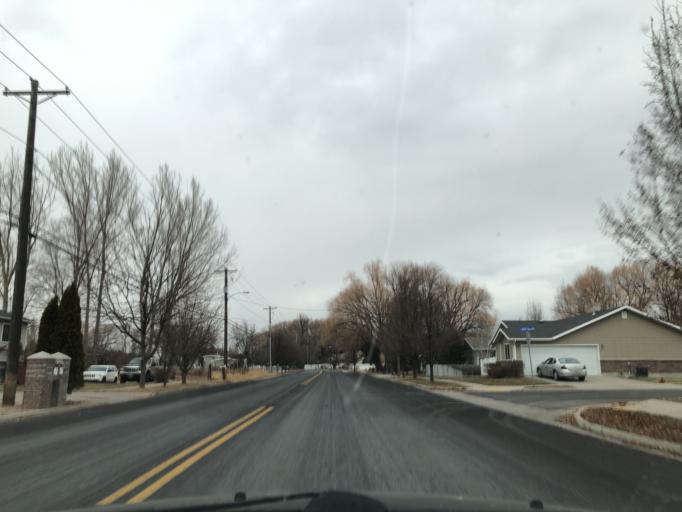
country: US
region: Utah
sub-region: Cache County
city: Logan
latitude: 41.7165
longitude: -111.8528
